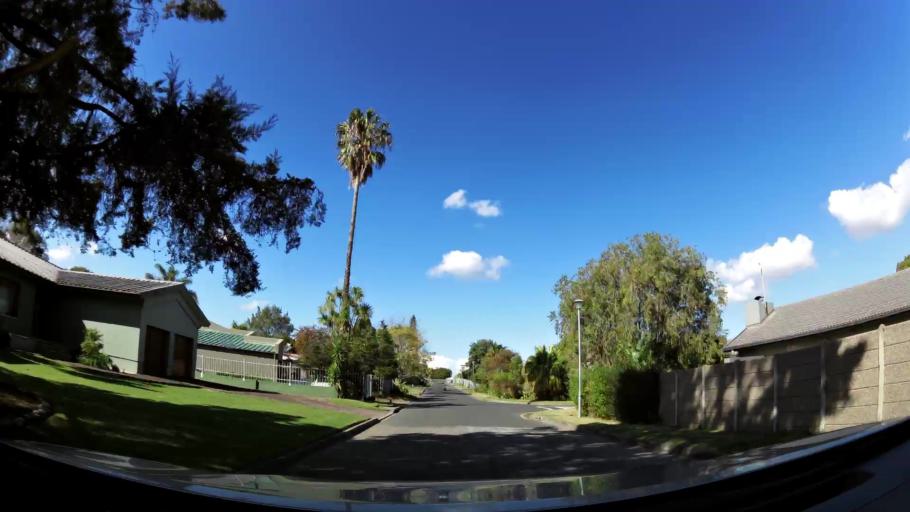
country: ZA
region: Western Cape
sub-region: Eden District Municipality
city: George
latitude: -33.9613
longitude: 22.4509
